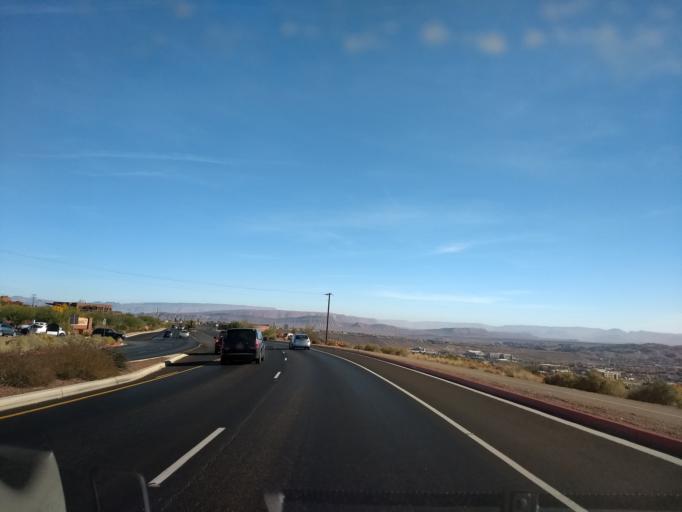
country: US
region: Utah
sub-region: Washington County
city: Saint George
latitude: 37.1147
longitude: -113.5784
